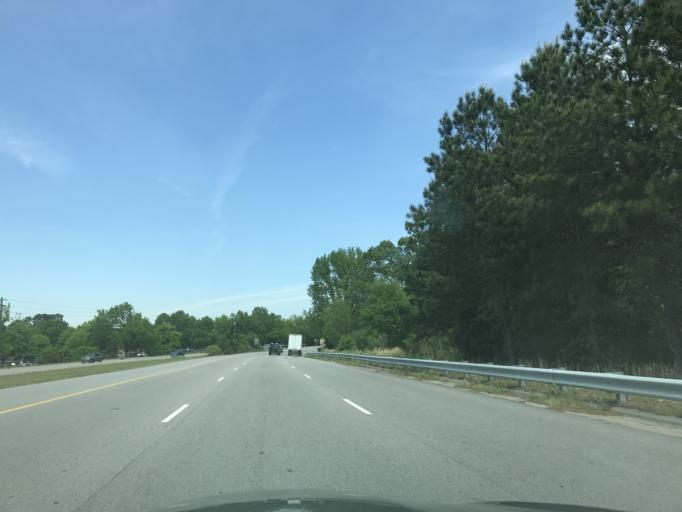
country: US
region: North Carolina
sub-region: Wake County
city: Raleigh
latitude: 35.8400
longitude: -78.5785
